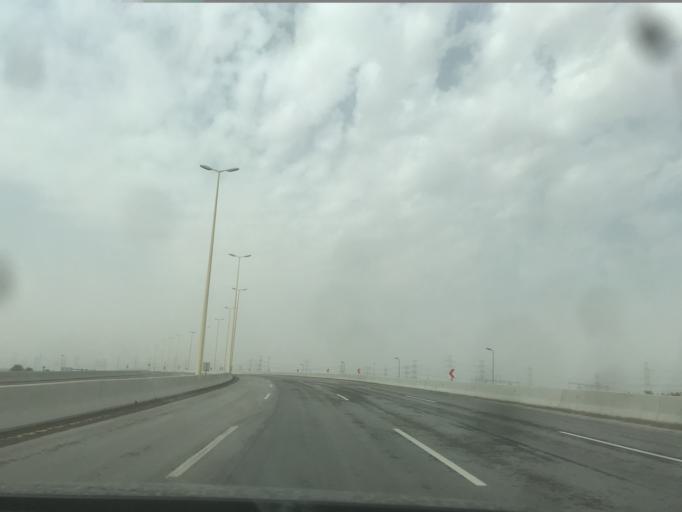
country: SA
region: Eastern Province
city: Dhahran
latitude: 26.2026
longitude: 50.0302
